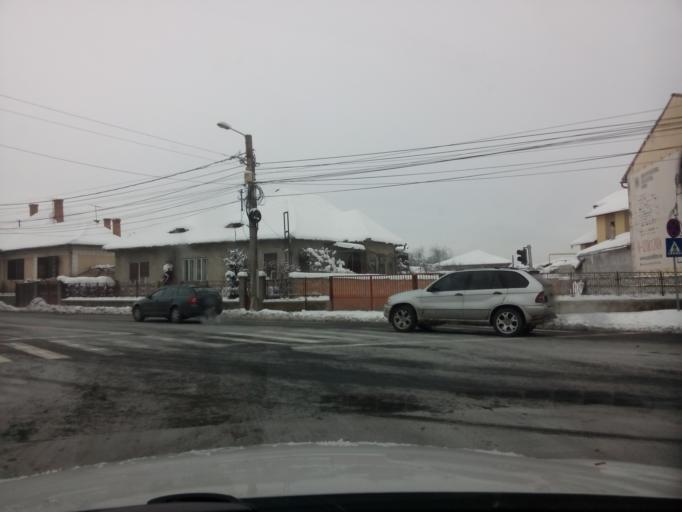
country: RO
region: Sibiu
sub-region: Municipiul Sibiu
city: Sibiu
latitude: 45.7901
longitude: 24.1643
